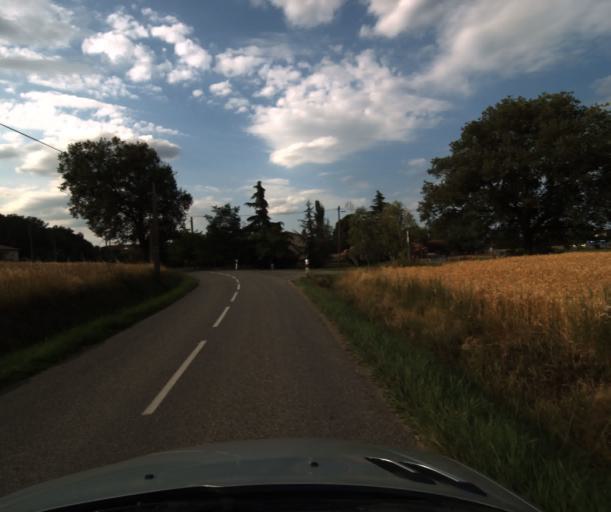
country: FR
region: Midi-Pyrenees
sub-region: Departement de la Haute-Garonne
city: Fonsorbes
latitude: 43.5264
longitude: 1.2325
